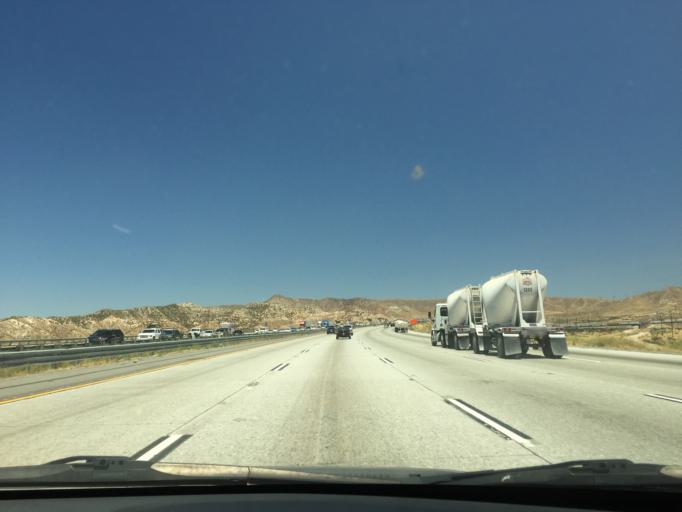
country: US
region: California
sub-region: San Bernardino County
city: Oak Hills
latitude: 34.3216
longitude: -117.4817
